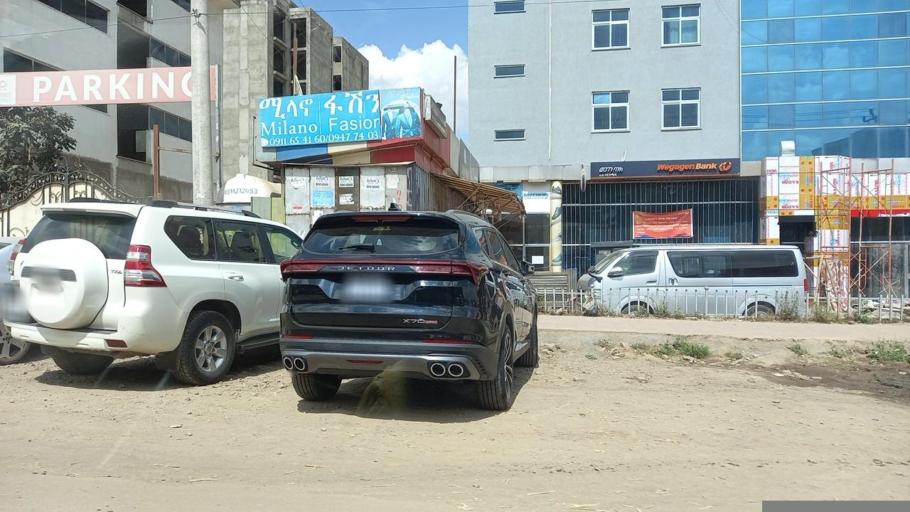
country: ET
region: Adis Abeba
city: Addis Ababa
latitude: 8.9485
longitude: 38.7320
